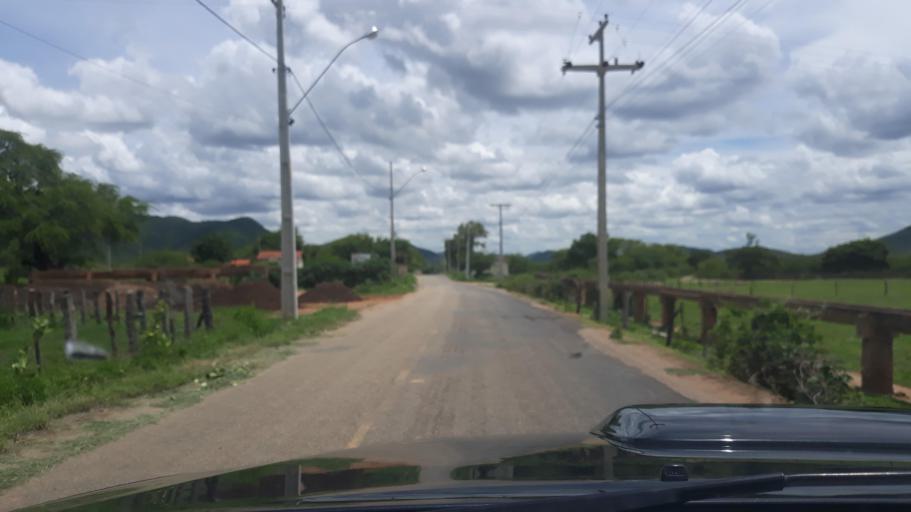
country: BR
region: Bahia
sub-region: Guanambi
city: Guanambi
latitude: -14.2941
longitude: -42.6969
